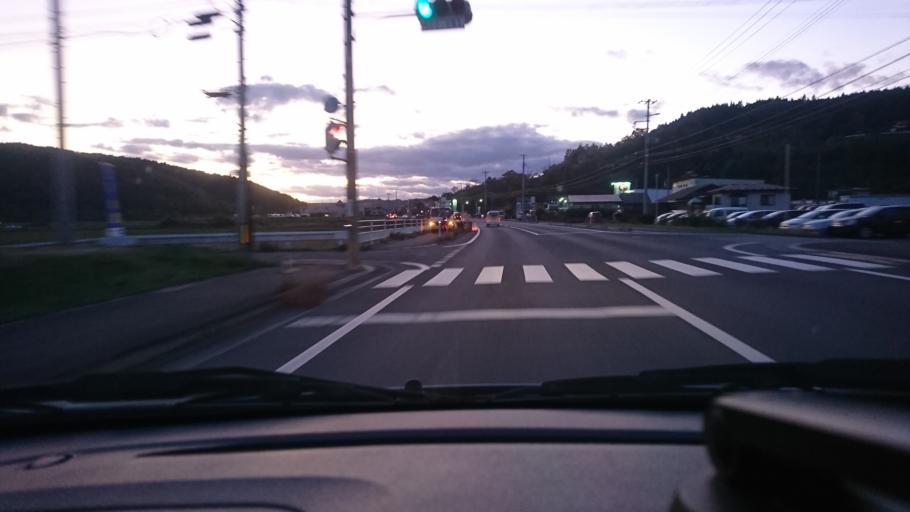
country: JP
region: Iwate
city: Ichinoseki
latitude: 38.9004
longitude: 141.2825
